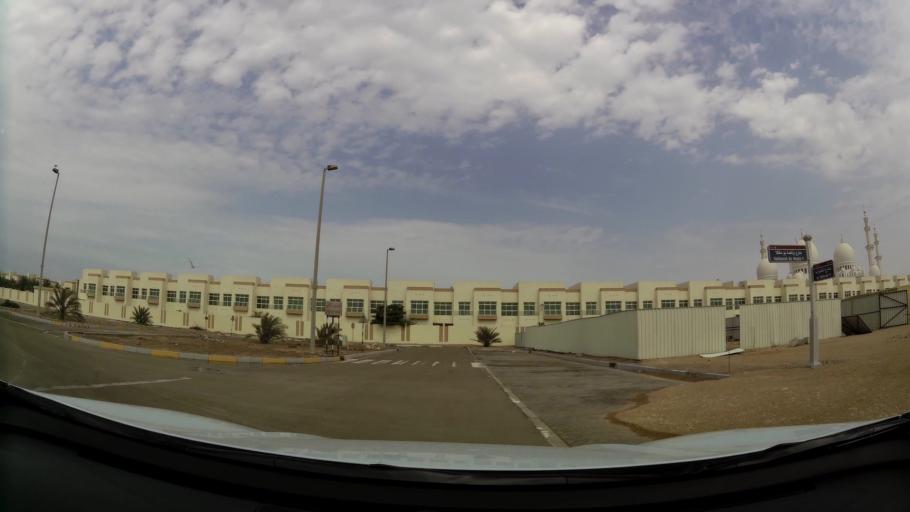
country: AE
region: Abu Dhabi
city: Abu Dhabi
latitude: 24.4103
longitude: 54.4700
